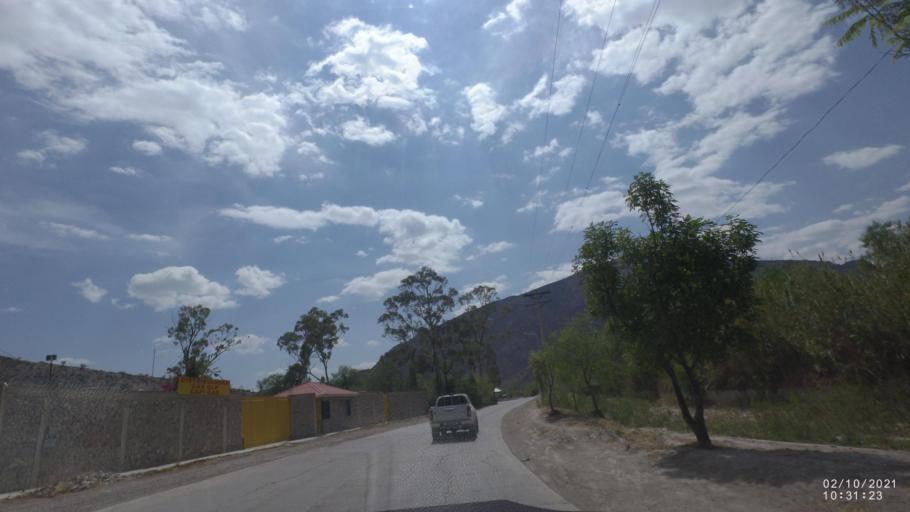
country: BO
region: Cochabamba
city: Capinota
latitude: -17.6947
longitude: -66.2605
